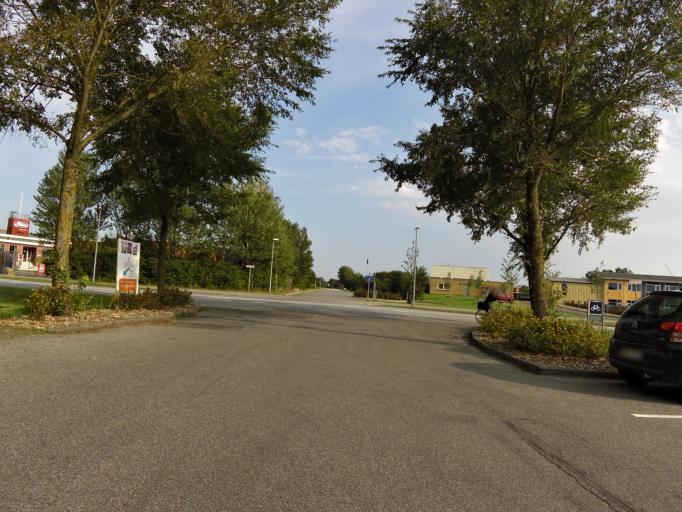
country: DK
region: South Denmark
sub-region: Esbjerg Kommune
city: Ribe
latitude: 55.3233
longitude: 8.7628
